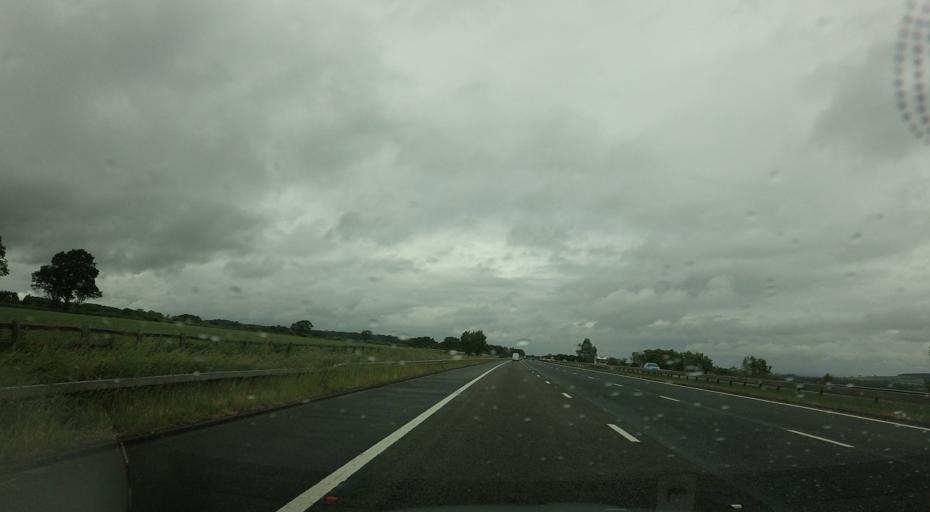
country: GB
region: England
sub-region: Cumbria
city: Scotby
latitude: 54.7764
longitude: -2.8514
